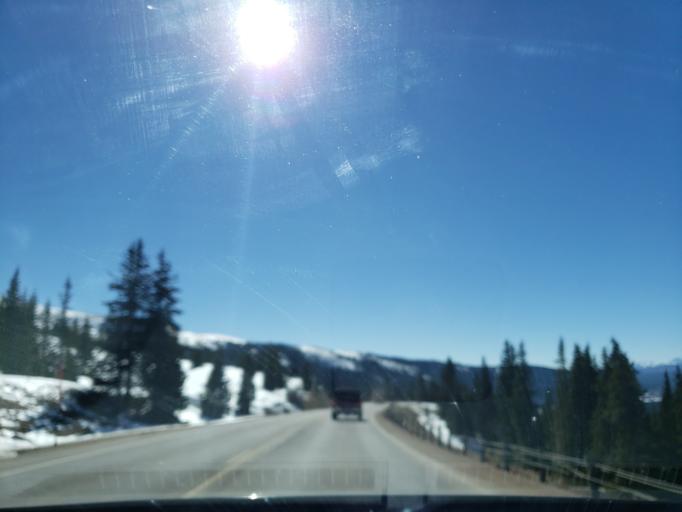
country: US
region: Colorado
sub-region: Summit County
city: Breckenridge
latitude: 39.3579
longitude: -106.0607
